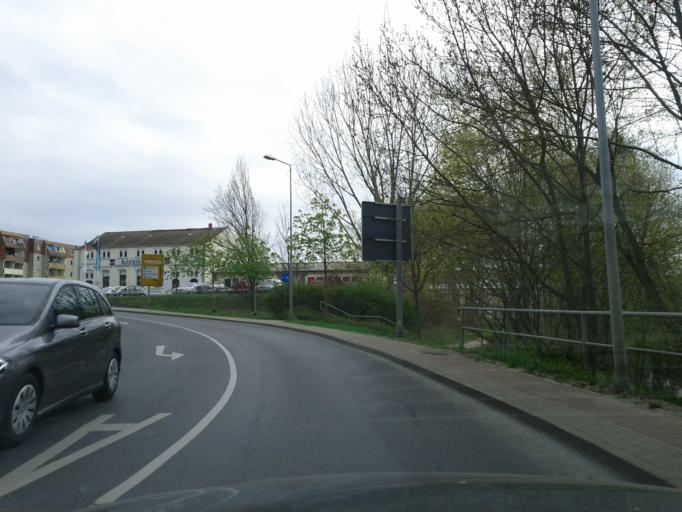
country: DE
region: Brandenburg
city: Furstenwalde
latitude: 52.3562
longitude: 14.0651
